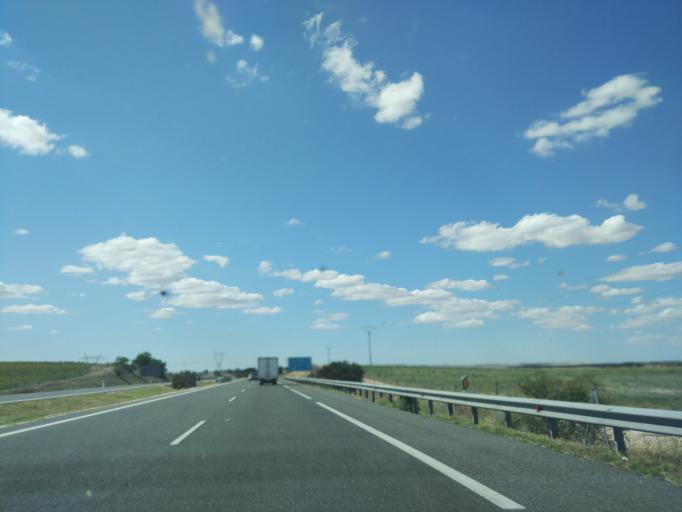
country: ES
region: Castille and Leon
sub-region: Provincia de Valladolid
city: San Vicente del Palacio
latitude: 41.2303
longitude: -4.8523
